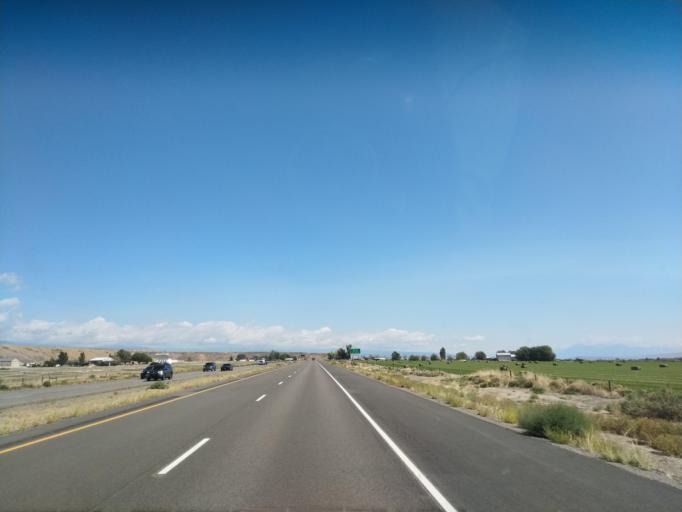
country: US
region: Colorado
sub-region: Delta County
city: Delta
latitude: 38.7567
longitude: -108.1476
